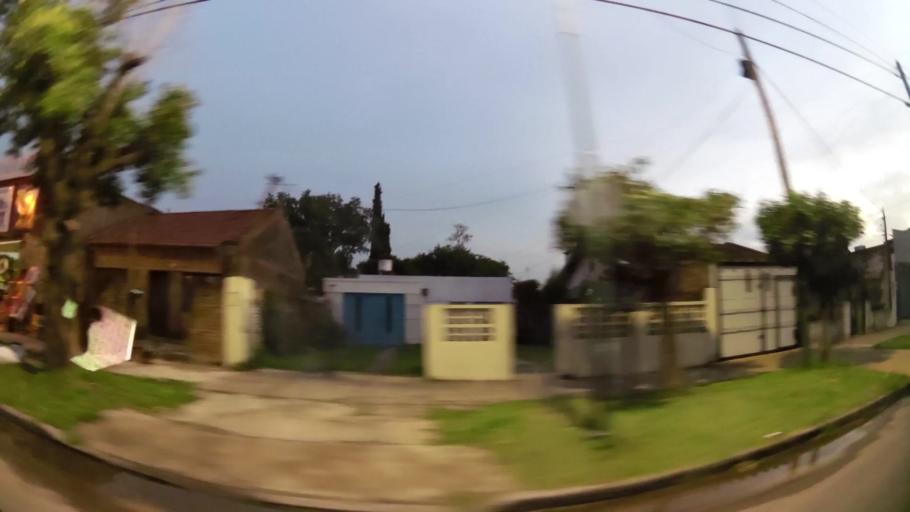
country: AR
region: Buenos Aires
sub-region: Partido de Lomas de Zamora
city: Lomas de Zamora
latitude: -34.7476
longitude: -58.3603
